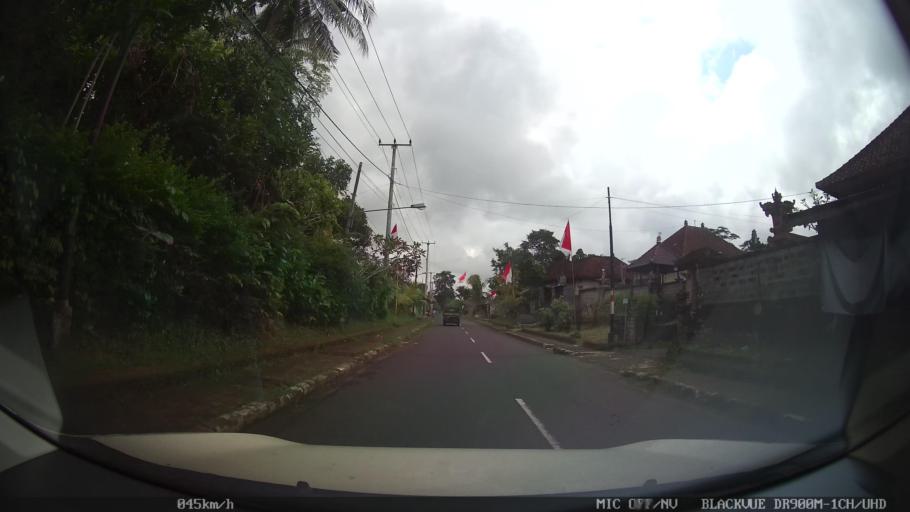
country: ID
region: Bali
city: Banjar Serangan
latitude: -8.5418
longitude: 115.1765
